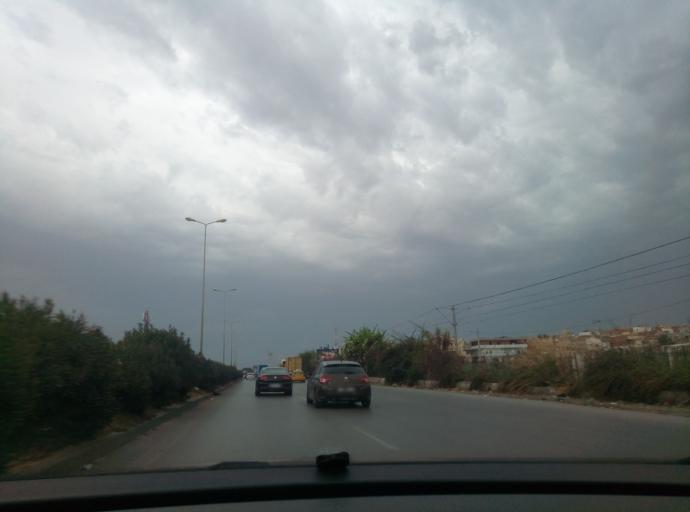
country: TN
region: Bin 'Arus
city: Ben Arous
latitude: 36.7535
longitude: 10.2033
